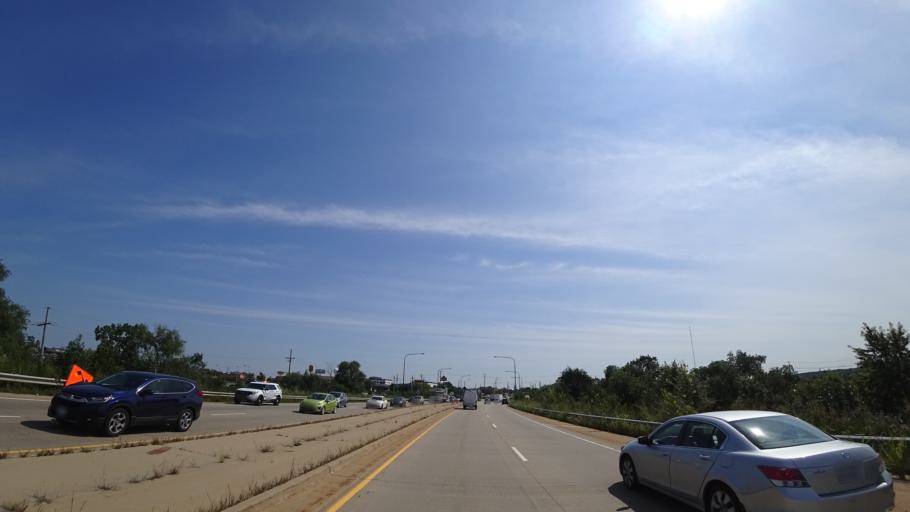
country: US
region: Illinois
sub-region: Cook County
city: Orland Hills
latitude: 41.5455
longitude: -87.8512
